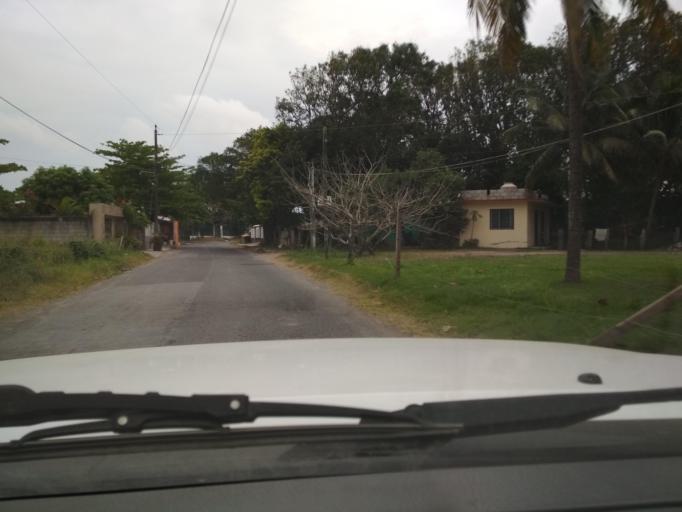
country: MX
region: Veracruz
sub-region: Medellin
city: Fraccionamiento Arboledas San Ramon
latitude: 19.0897
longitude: -96.1323
